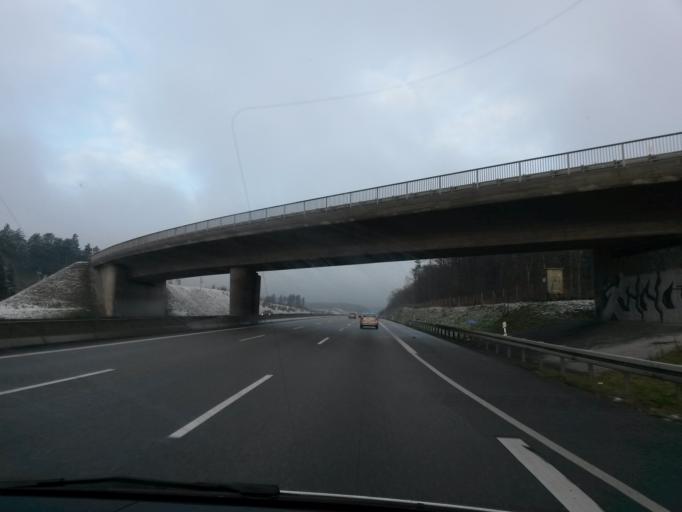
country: DE
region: Baden-Wuerttemberg
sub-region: Regierungsbezirk Stuttgart
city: Rutesheim
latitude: 48.8122
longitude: 8.9202
